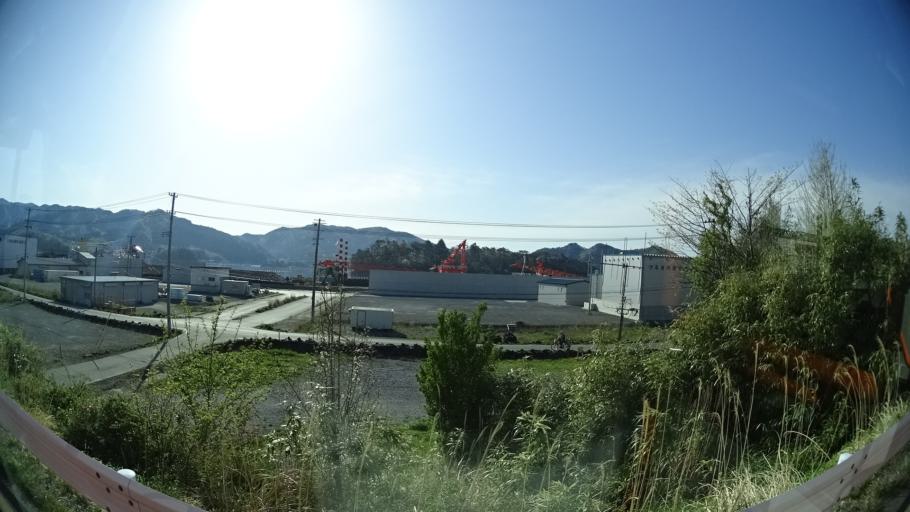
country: JP
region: Iwate
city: Ofunato
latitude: 39.0400
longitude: 141.7226
